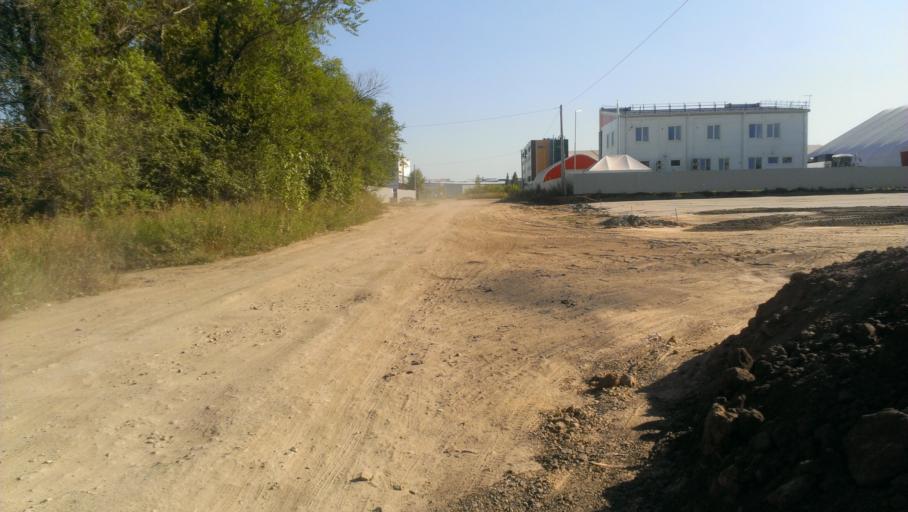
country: RU
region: Altai Krai
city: Novosilikatnyy
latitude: 53.3356
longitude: 83.6647
